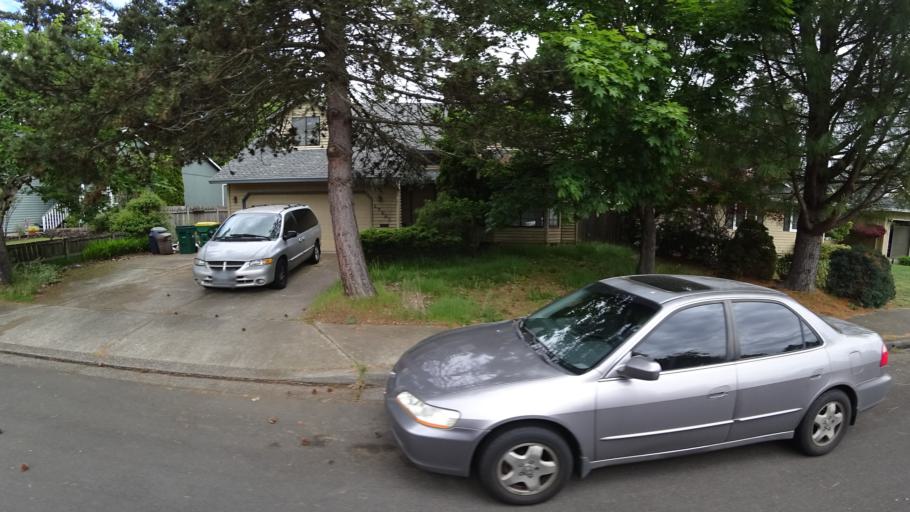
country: US
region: Oregon
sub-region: Washington County
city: Aloha
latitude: 45.4653
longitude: -122.8558
